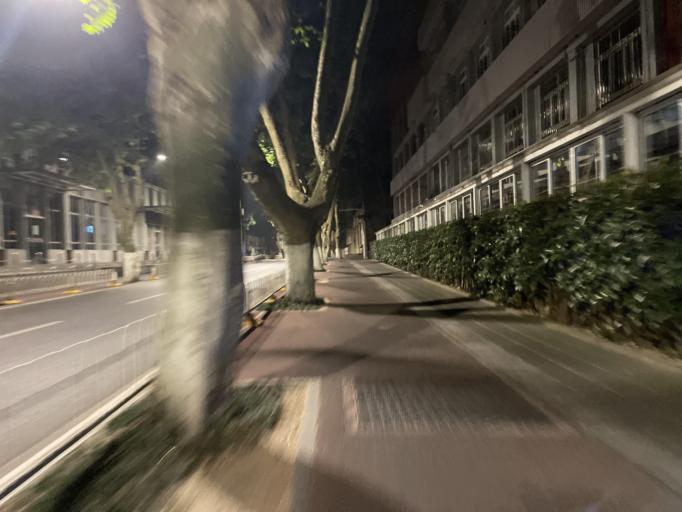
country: CN
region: Hubei
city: Guanshan
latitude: 30.5183
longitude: 114.4088
